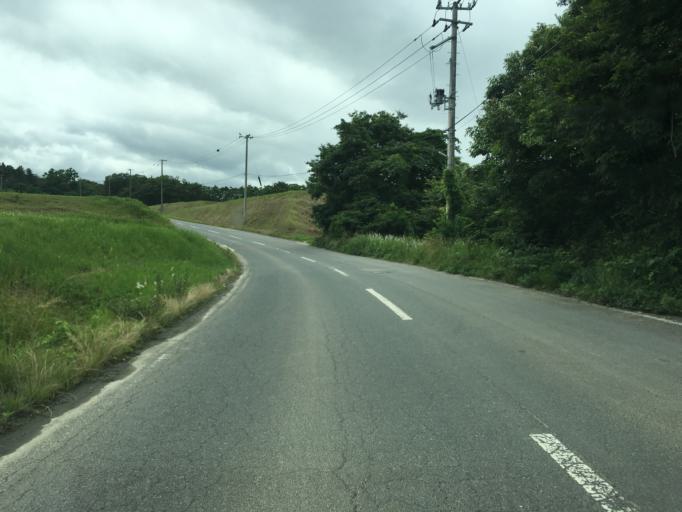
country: JP
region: Miyagi
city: Marumori
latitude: 37.7441
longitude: 140.9349
